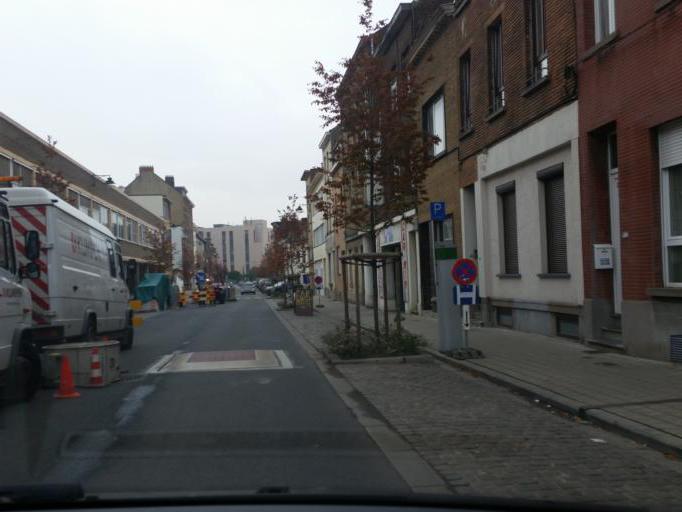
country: BE
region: Flanders
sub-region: Provincie Vlaams-Brabant
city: Drogenbos
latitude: 50.8122
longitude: 4.3190
